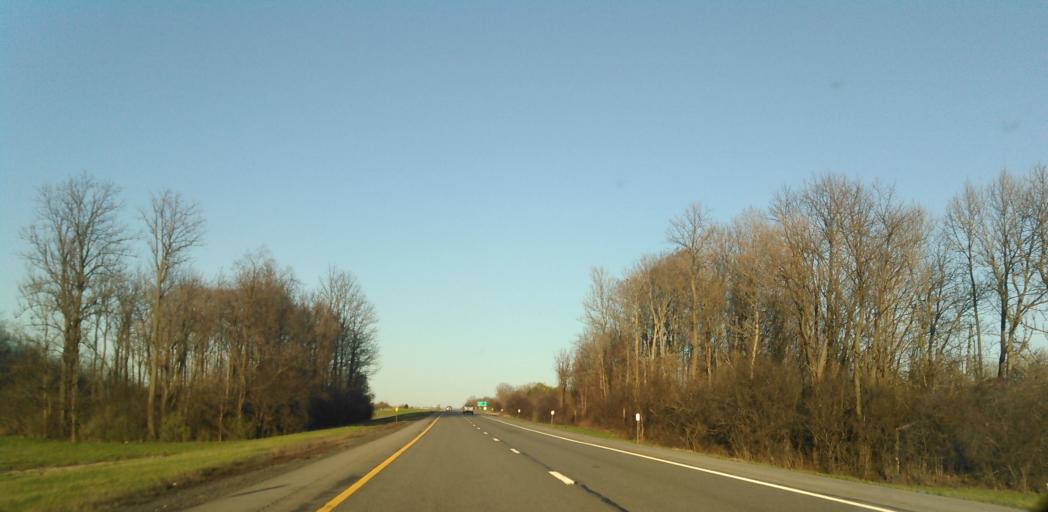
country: US
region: New York
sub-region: Monroe County
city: Honeoye Falls
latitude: 43.0467
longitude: -77.6104
